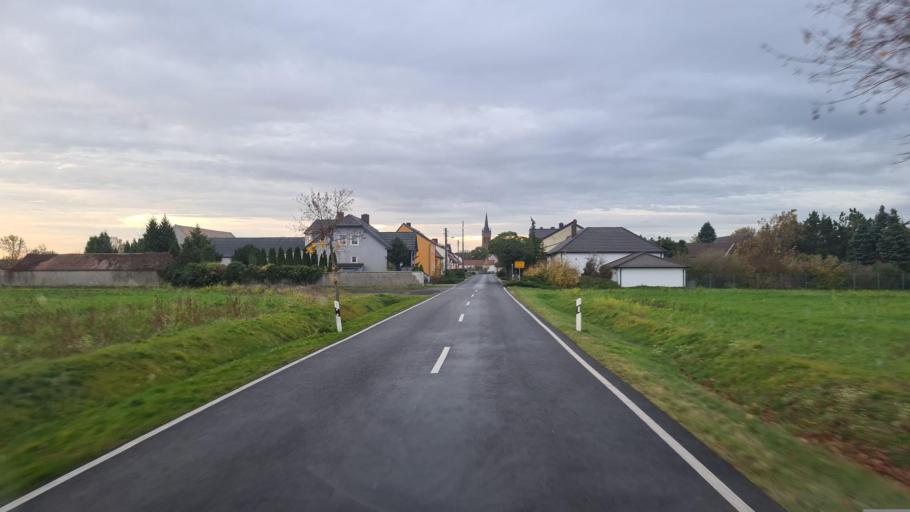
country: DE
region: Saxony-Anhalt
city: Holzdorf
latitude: 51.7823
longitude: 13.1297
